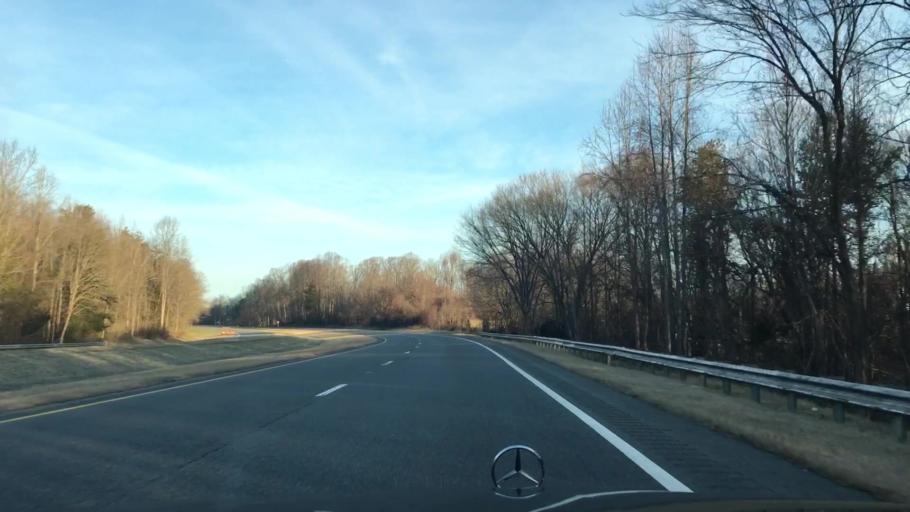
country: US
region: North Carolina
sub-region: Guilford County
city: Greensboro
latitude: 36.0216
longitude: -79.7638
